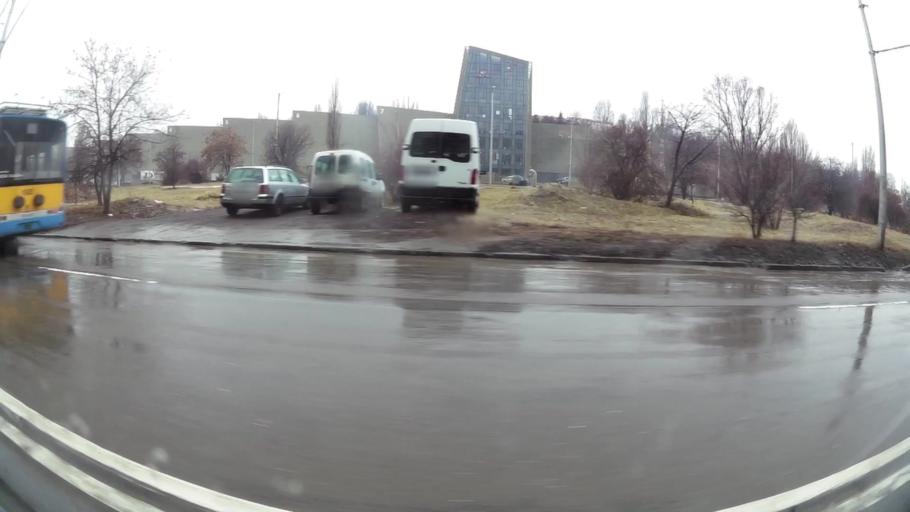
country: BG
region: Sofia-Capital
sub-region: Stolichna Obshtina
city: Sofia
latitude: 42.6669
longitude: 23.3872
